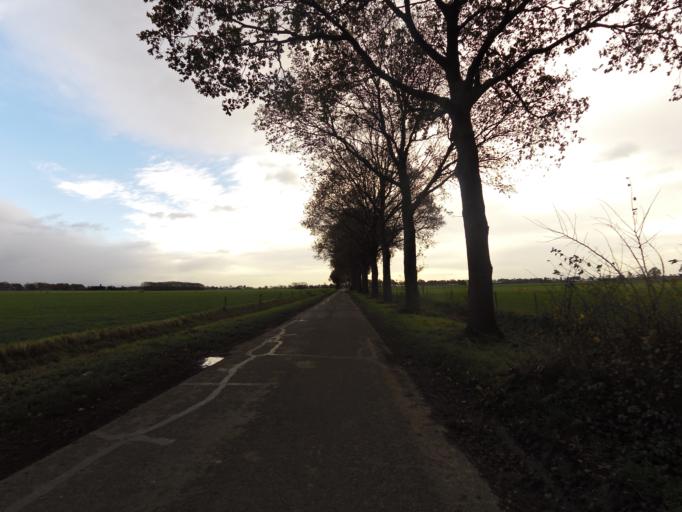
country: NL
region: Gelderland
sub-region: Gemeente Montferland
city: s-Heerenberg
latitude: 51.8948
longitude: 6.2784
